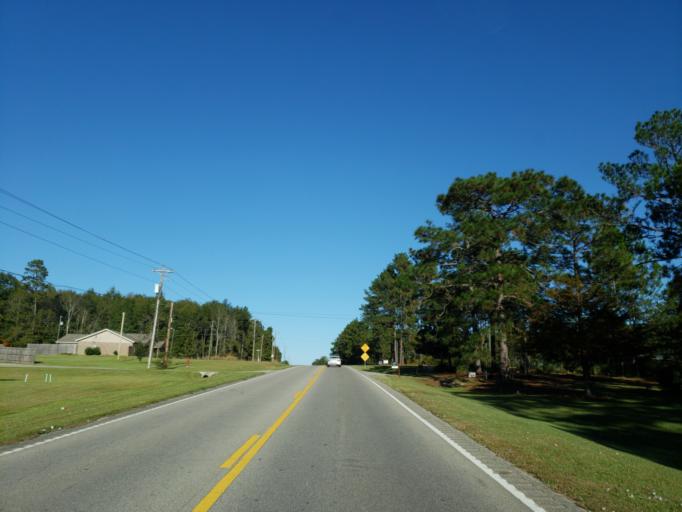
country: US
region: Mississippi
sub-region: Forrest County
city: Petal
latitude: 31.3533
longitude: -89.1699
